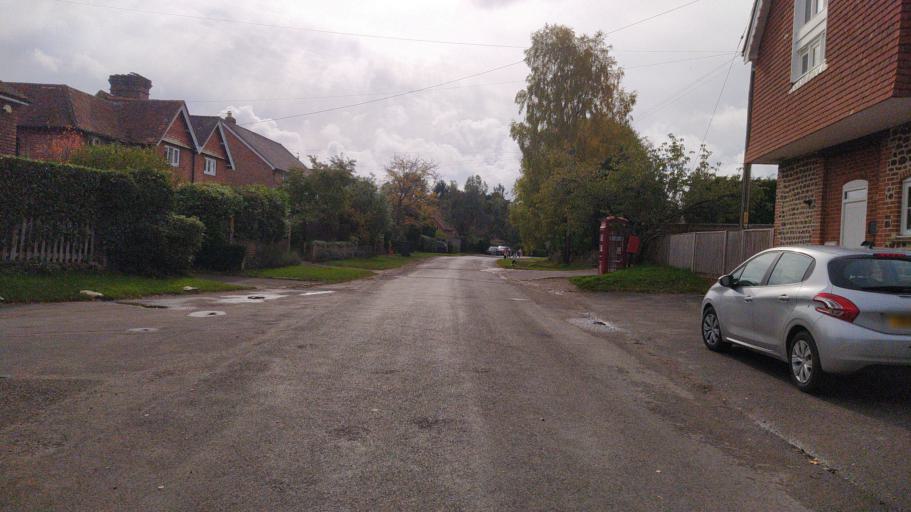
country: GB
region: England
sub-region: West Sussex
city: Midhurst
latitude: 50.9941
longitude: -0.7725
